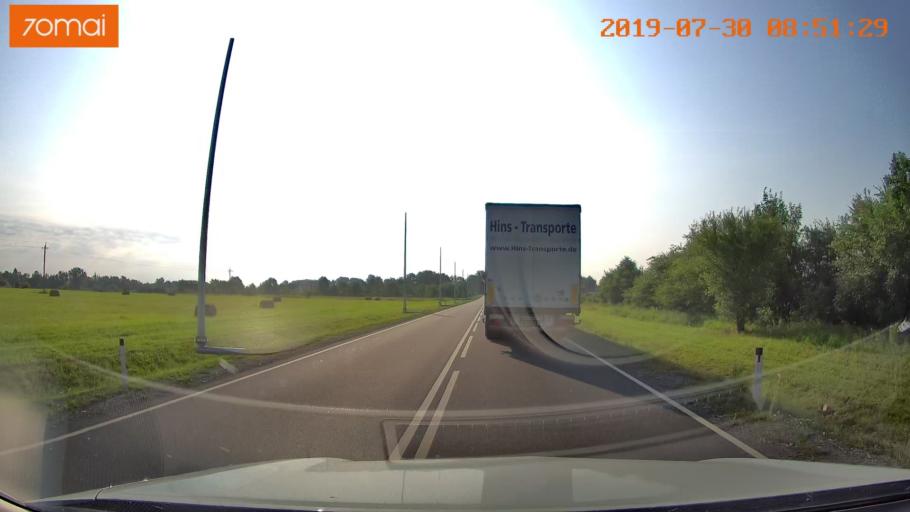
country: RU
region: Kaliningrad
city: Chernyakhovsk
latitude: 54.6022
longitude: 21.9588
